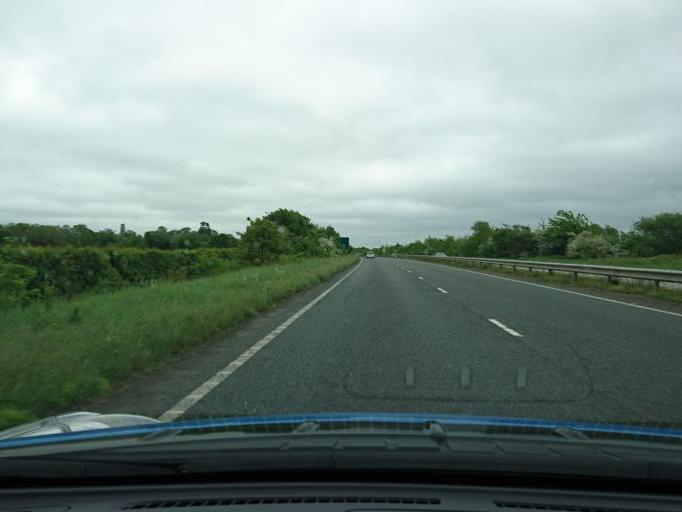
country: GB
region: England
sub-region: Oxfordshire
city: Stanford in the Vale
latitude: 51.6758
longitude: -1.4501
